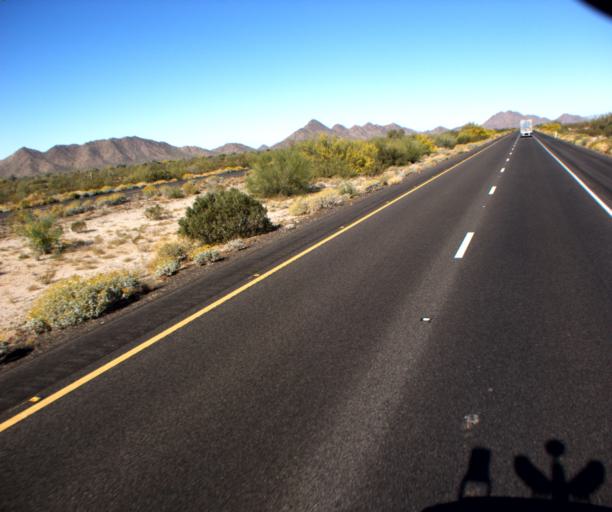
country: US
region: Arizona
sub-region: Maricopa County
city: Gila Bend
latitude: 32.8877
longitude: -112.4747
